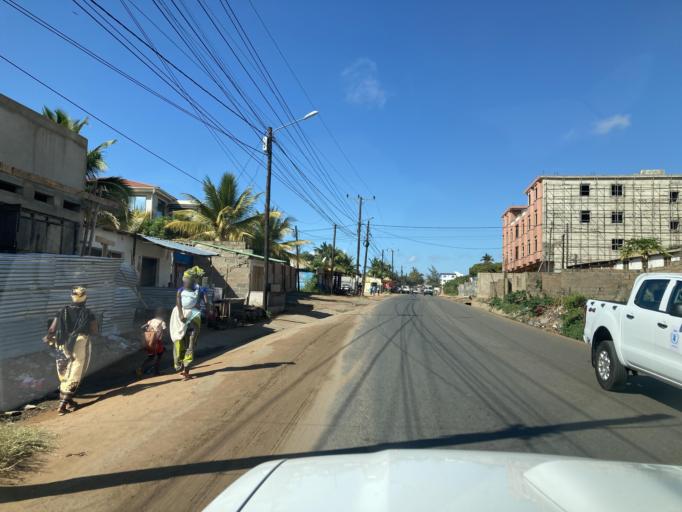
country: MZ
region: Cabo Delgado
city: Pemba
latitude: -12.9773
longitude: 40.5414
